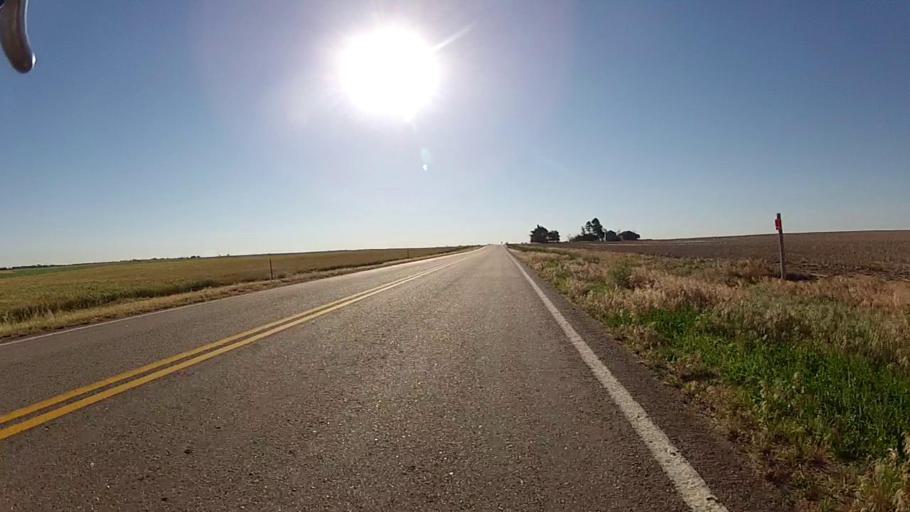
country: US
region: Kansas
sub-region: Ford County
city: Dodge City
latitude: 37.6461
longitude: -99.8184
